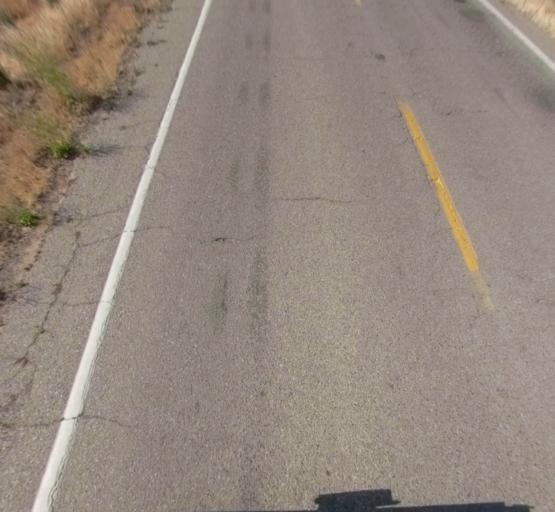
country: US
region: California
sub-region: Madera County
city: Fairmead
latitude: 36.9938
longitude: -120.2562
